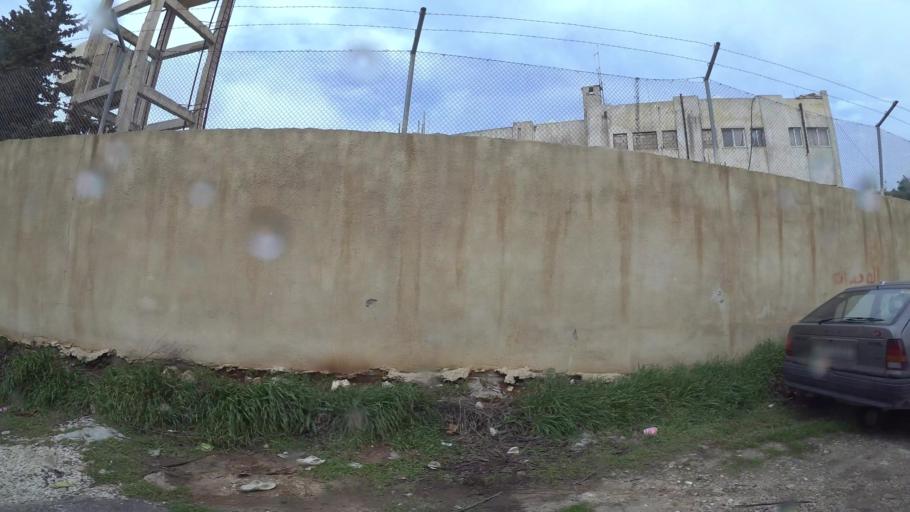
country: JO
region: Amman
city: Umm as Summaq
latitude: 31.8937
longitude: 35.8605
